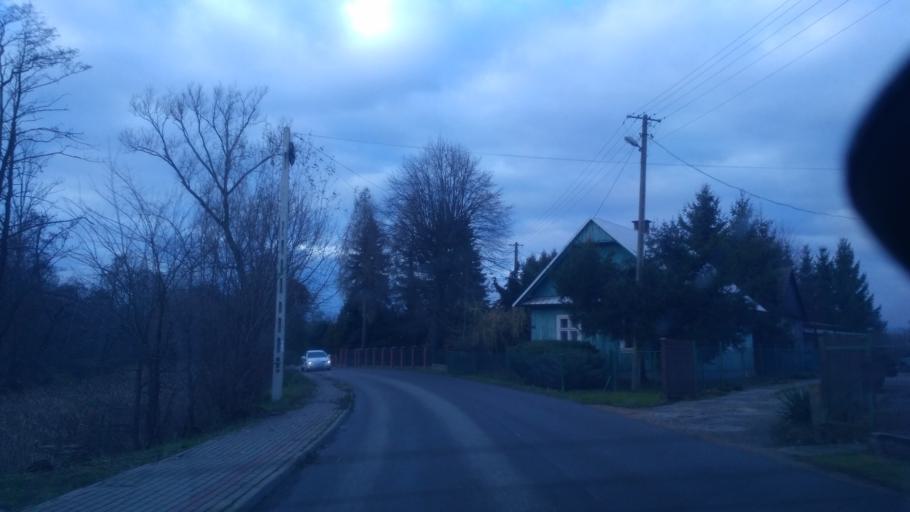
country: PL
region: Subcarpathian Voivodeship
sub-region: Powiat rzeszowski
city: Krasne
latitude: 50.0706
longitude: 22.1157
